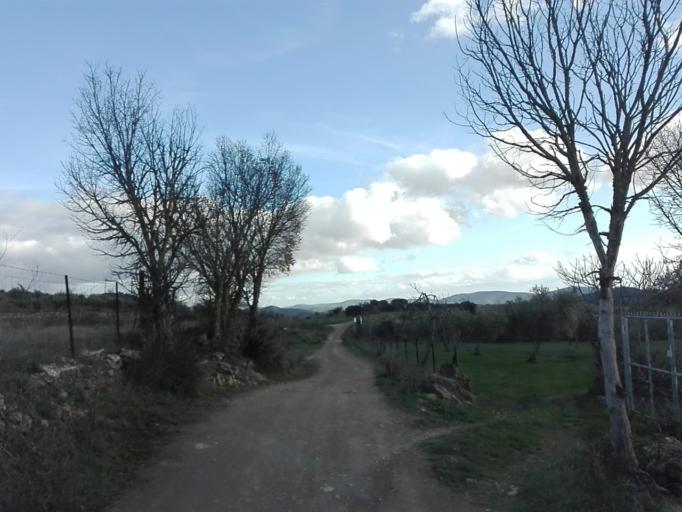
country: ES
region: Extremadura
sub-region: Provincia de Badajoz
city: Trasierra
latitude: 38.1858
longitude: -5.9871
